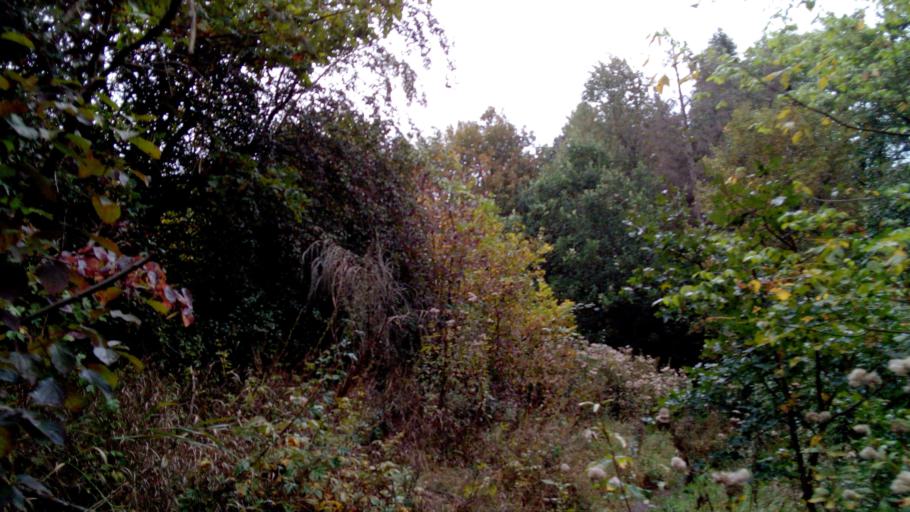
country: DE
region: North Rhine-Westphalia
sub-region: Regierungsbezirk Arnsberg
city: Bochum
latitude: 51.4426
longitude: 7.2501
